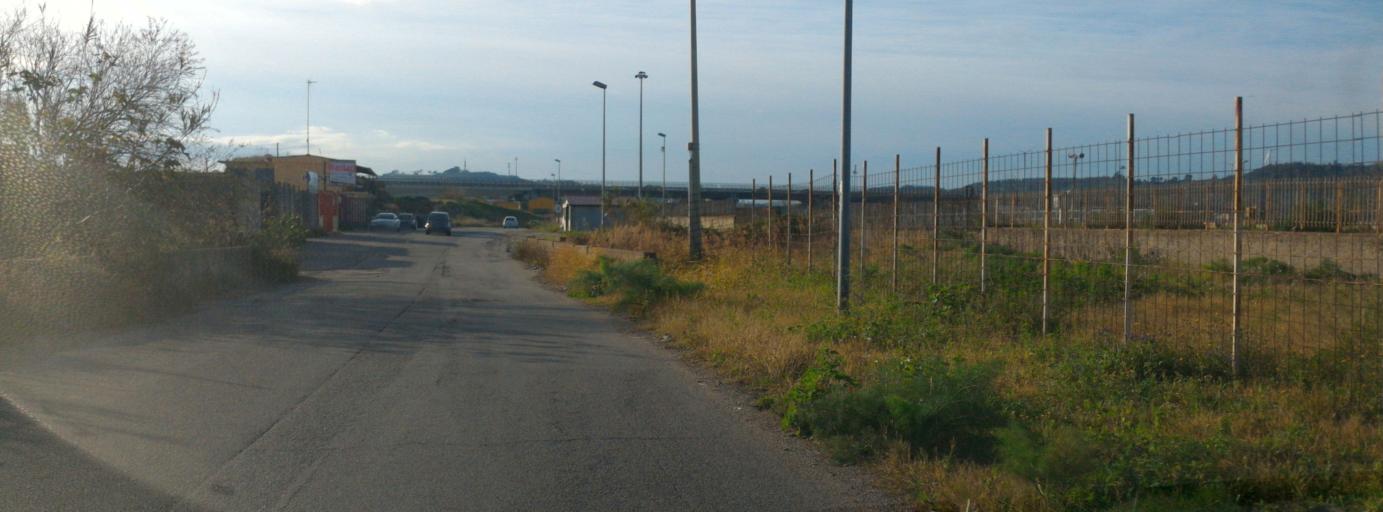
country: IT
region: Calabria
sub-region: Provincia di Crotone
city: Crotone
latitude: 39.0904
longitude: 17.1126
